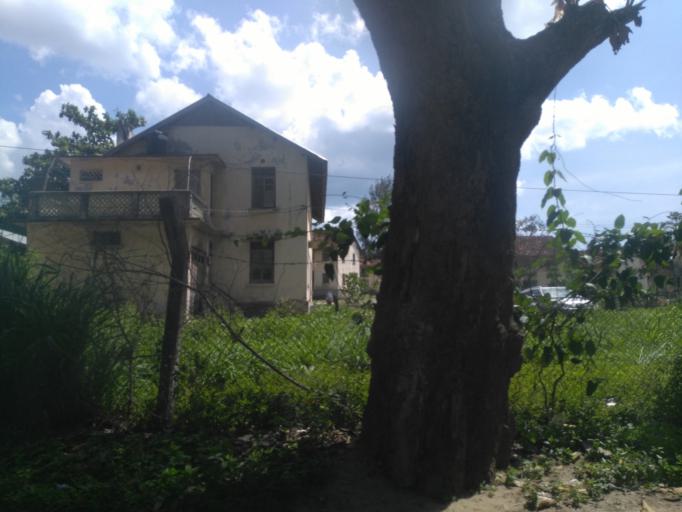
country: TZ
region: Zanzibar Urban/West
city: Zanzibar
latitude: -6.1698
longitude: 39.2063
